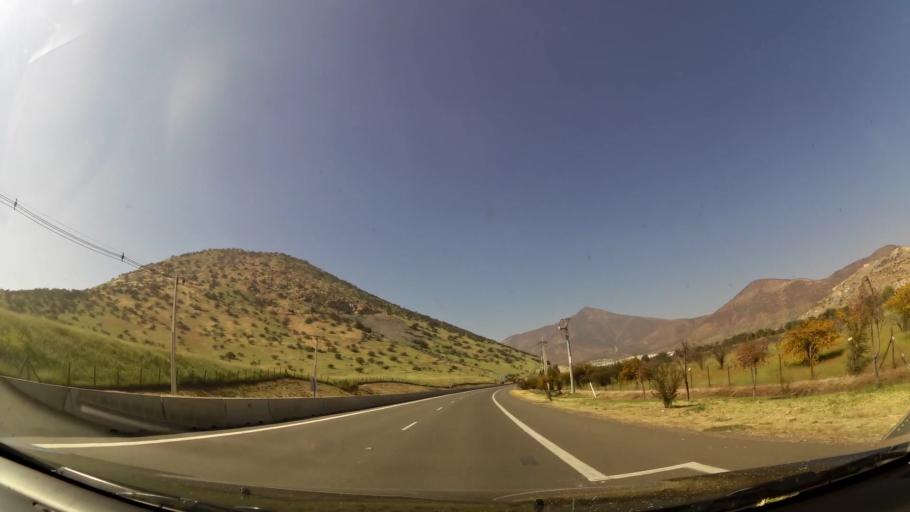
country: CL
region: Santiago Metropolitan
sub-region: Provincia de Chacabuco
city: Chicureo Abajo
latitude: -33.3043
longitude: -70.6556
